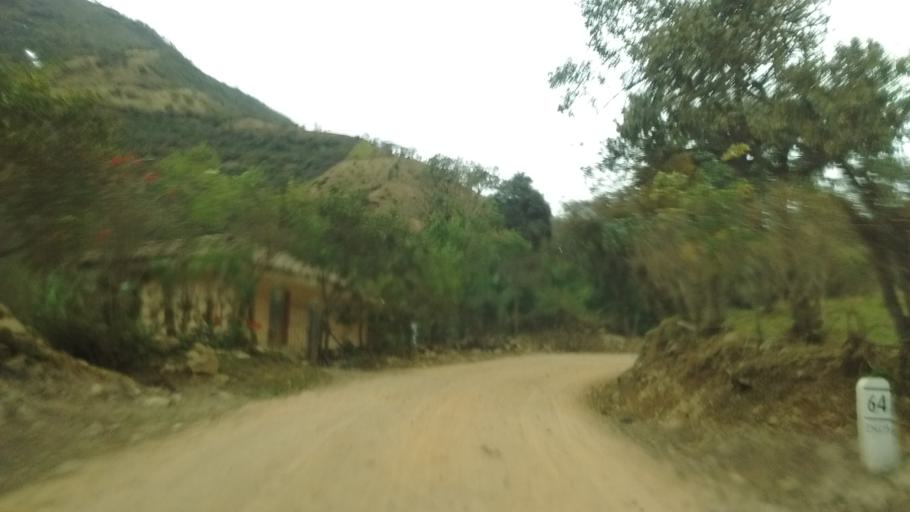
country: CO
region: Cauca
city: La Vega
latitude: 2.0110
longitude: -76.7907
